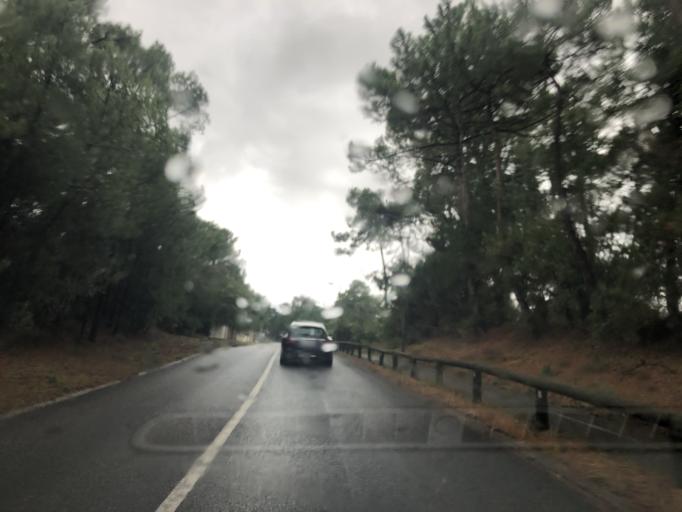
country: FR
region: Aquitaine
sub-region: Departement de la Gironde
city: Arcachon
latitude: 44.6910
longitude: -1.2396
